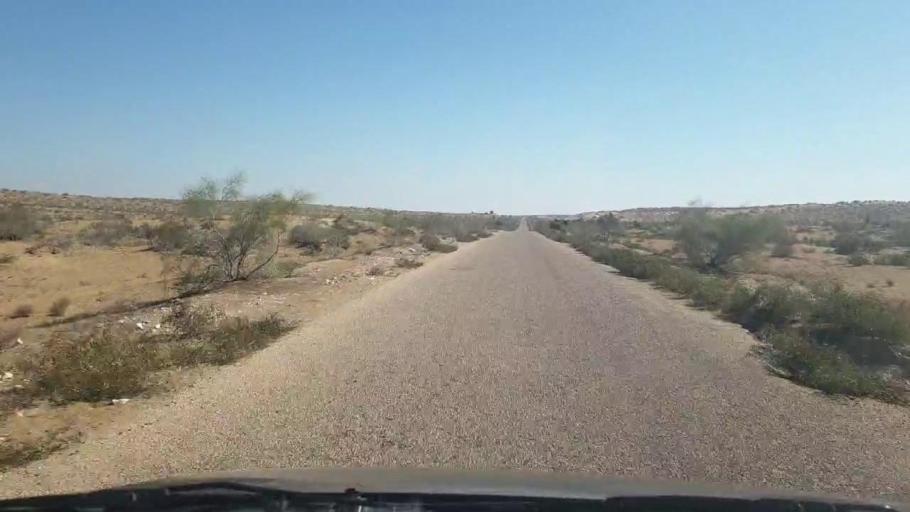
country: PK
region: Sindh
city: Bozdar
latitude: 27.0194
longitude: 68.7735
